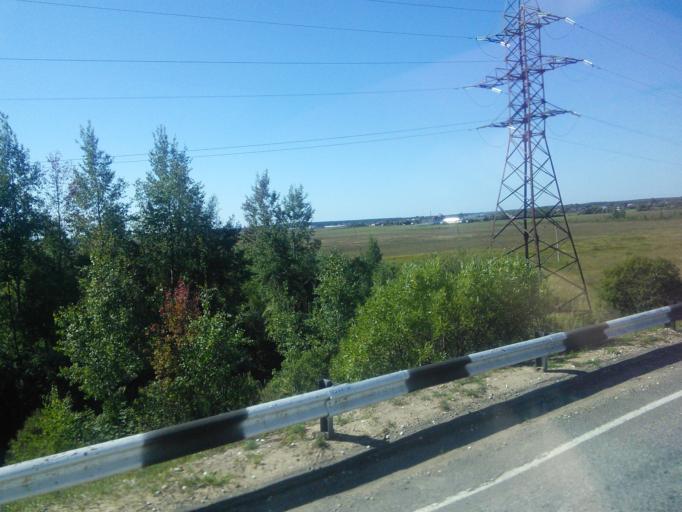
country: RU
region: Tverskaya
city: Kalyazin
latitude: 57.2330
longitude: 37.7905
